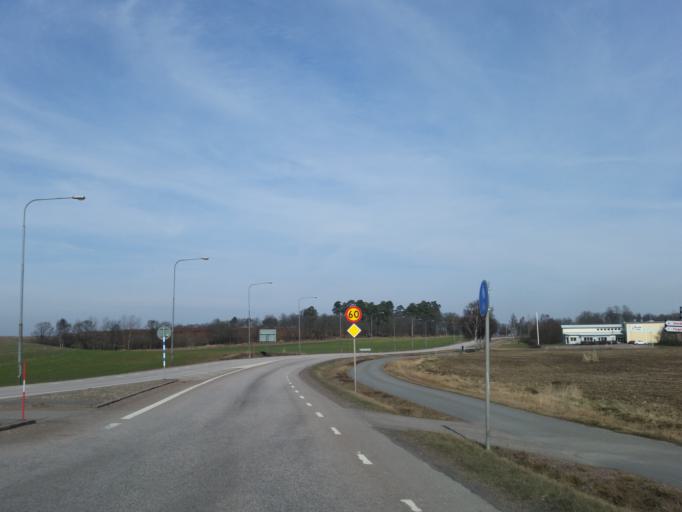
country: SE
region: Kalmar
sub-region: Kalmar Kommun
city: Rinkabyholm
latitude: 56.6733
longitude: 16.3027
